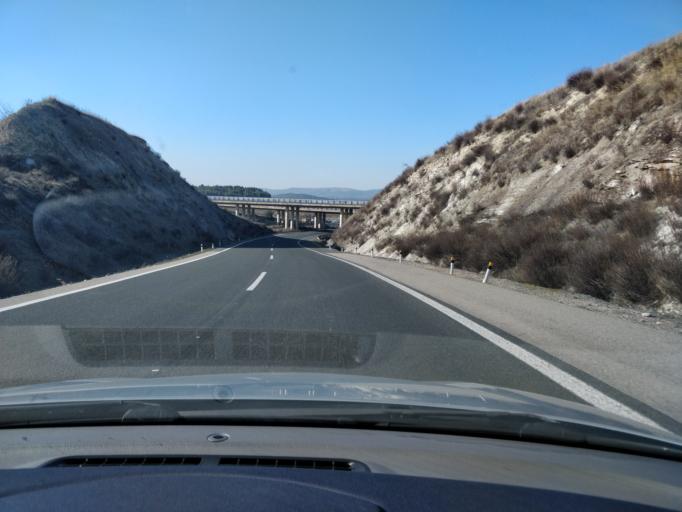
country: ES
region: Basque Country
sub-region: Provincia de Alava
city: Arminon
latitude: 42.7090
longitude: -2.9017
